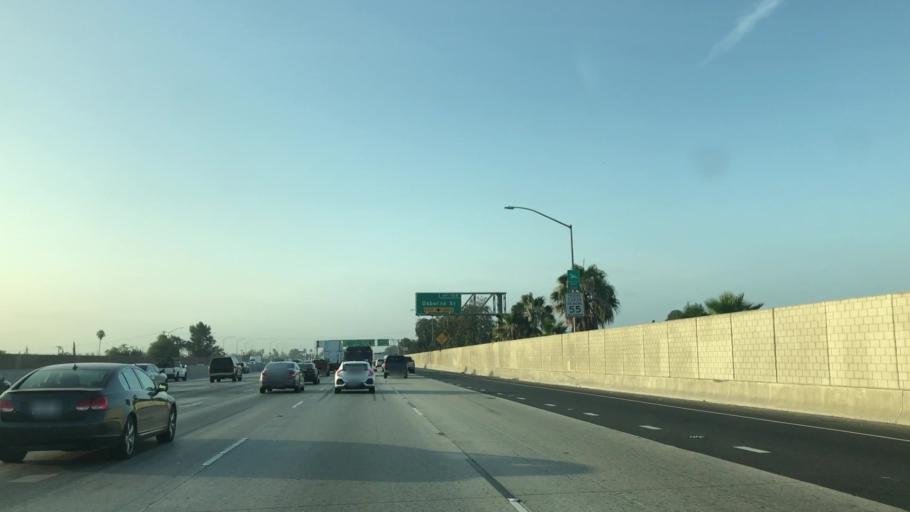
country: US
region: California
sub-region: Los Angeles County
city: San Fernando
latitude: 34.2410
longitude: -118.4224
